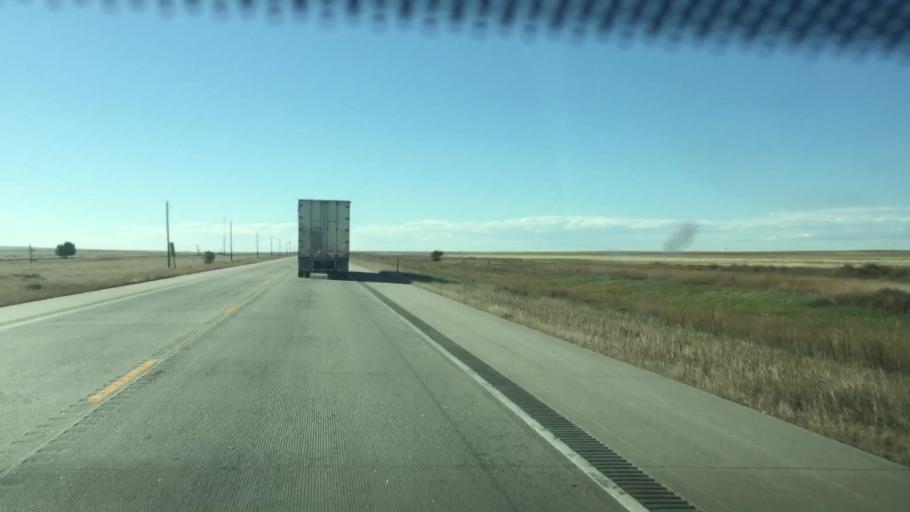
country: US
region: Colorado
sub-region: Kiowa County
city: Eads
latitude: 38.8297
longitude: -103.0356
